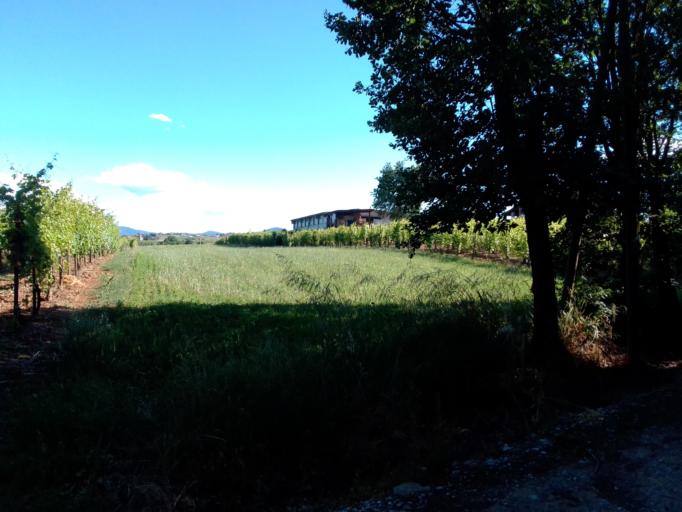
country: IT
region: Emilia-Romagna
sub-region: Provincia di Piacenza
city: Ziano Piacentino
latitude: 45.0064
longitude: 9.4170
